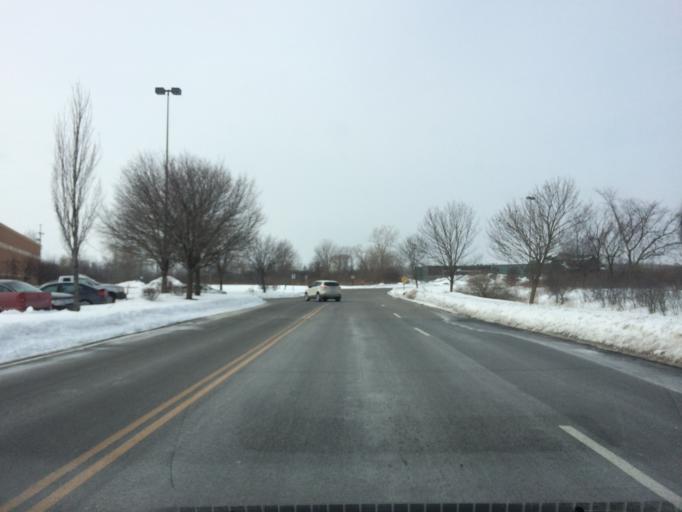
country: US
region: New York
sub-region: Monroe County
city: Rochester
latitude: 43.0800
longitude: -77.6319
